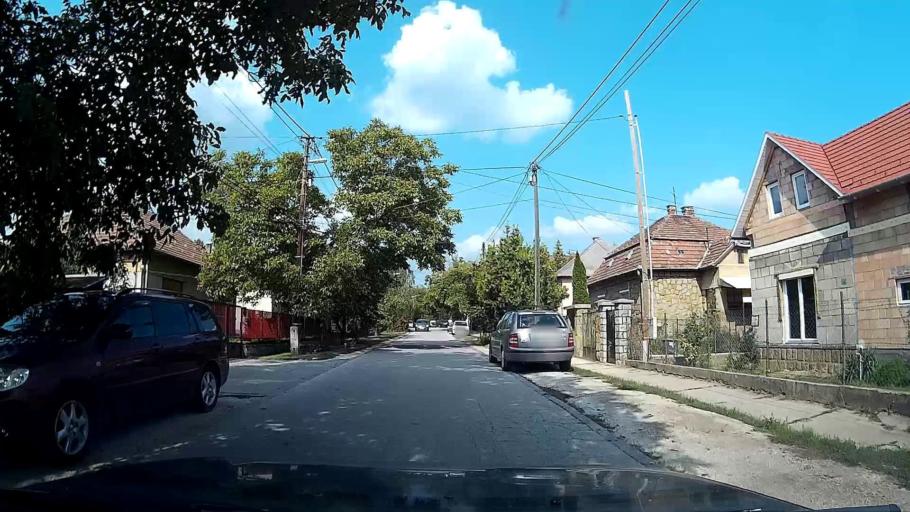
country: HU
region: Pest
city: Budakeszi
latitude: 47.5089
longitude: 18.9215
